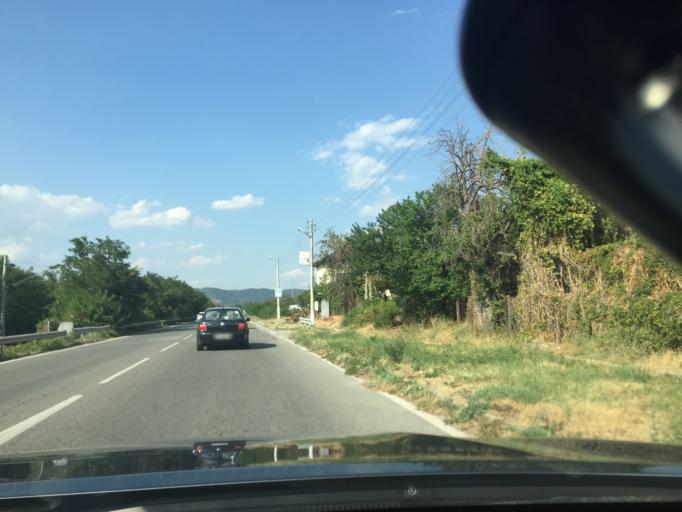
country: BG
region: Kyustendil
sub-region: Obshtina Dupnitsa
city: Dupnitsa
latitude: 42.2272
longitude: 23.0814
